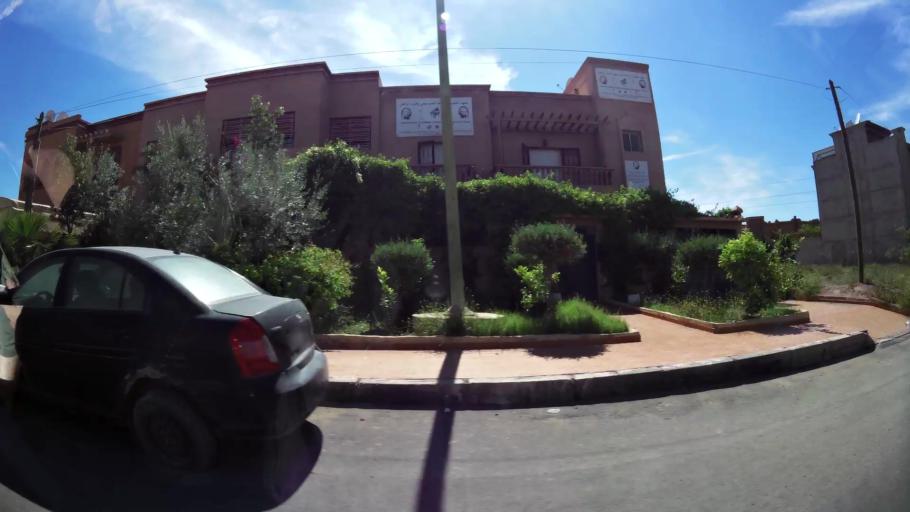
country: MA
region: Marrakech-Tensift-Al Haouz
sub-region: Marrakech
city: Marrakesh
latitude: 31.6410
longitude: -8.0415
